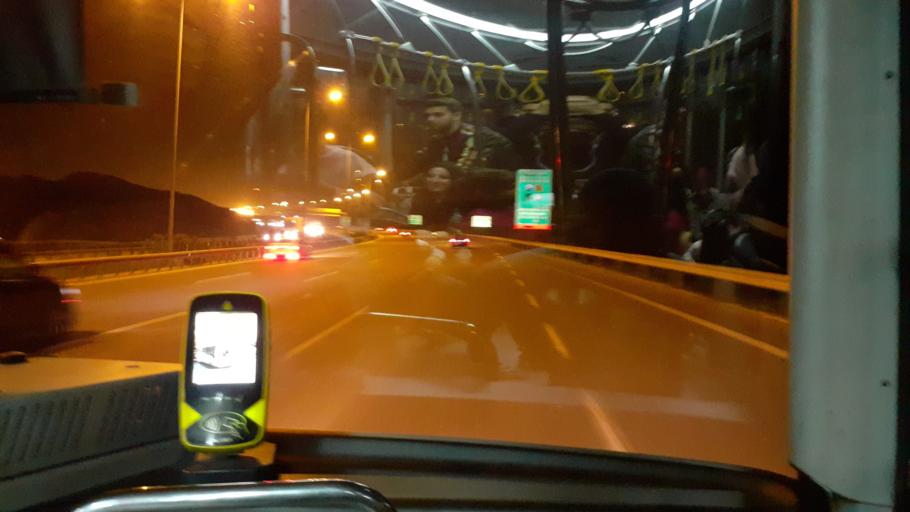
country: TR
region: Istanbul
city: Kemerburgaz
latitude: 41.2097
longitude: 28.8247
